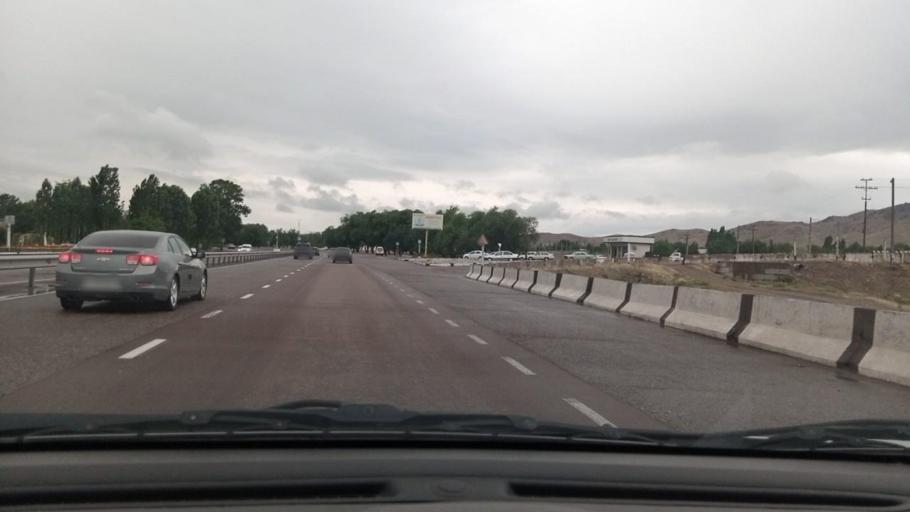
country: UZ
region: Toshkent
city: Ohangaron
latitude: 40.9087
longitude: 69.7925
